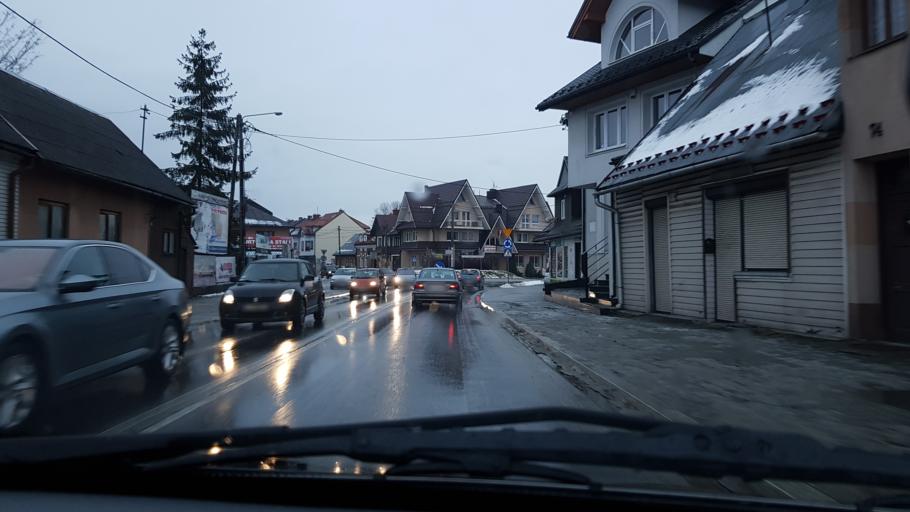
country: PL
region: Lesser Poland Voivodeship
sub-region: Powiat nowotarski
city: Nowy Targ
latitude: 49.4810
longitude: 20.0416
